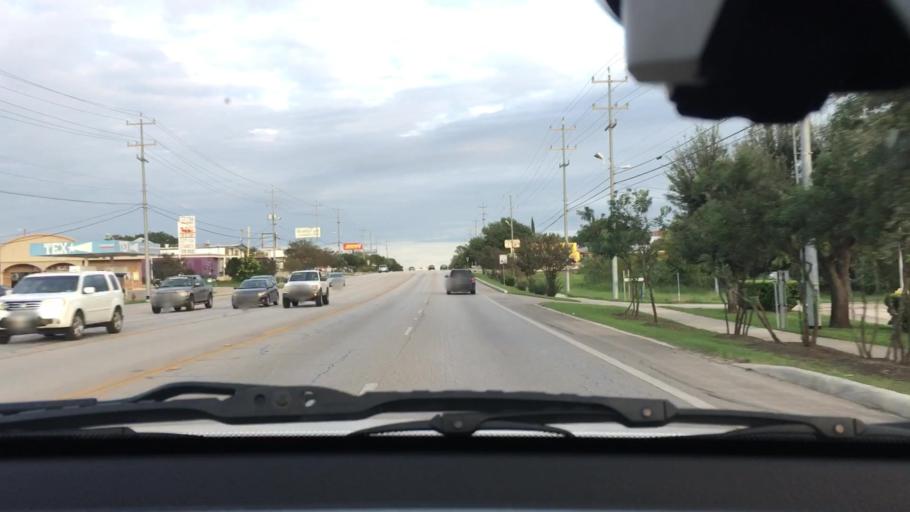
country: US
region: Texas
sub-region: Bexar County
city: Universal City
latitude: 29.5520
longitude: -98.3039
